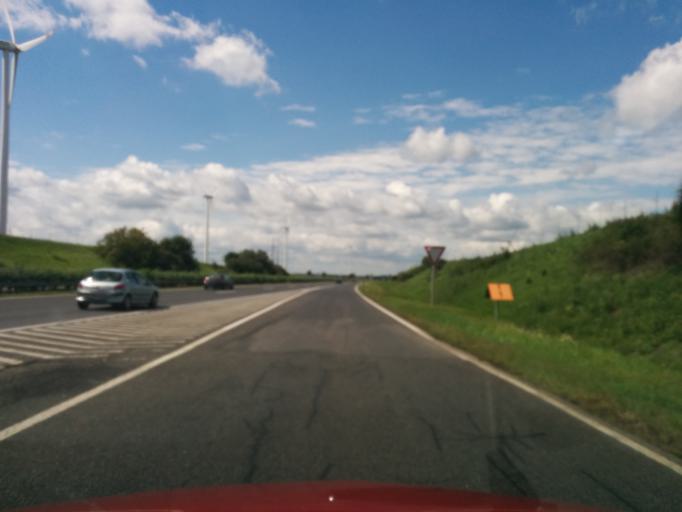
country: HU
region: Komarom-Esztergom
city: Nagyigmand
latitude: 47.6747
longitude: 18.0878
